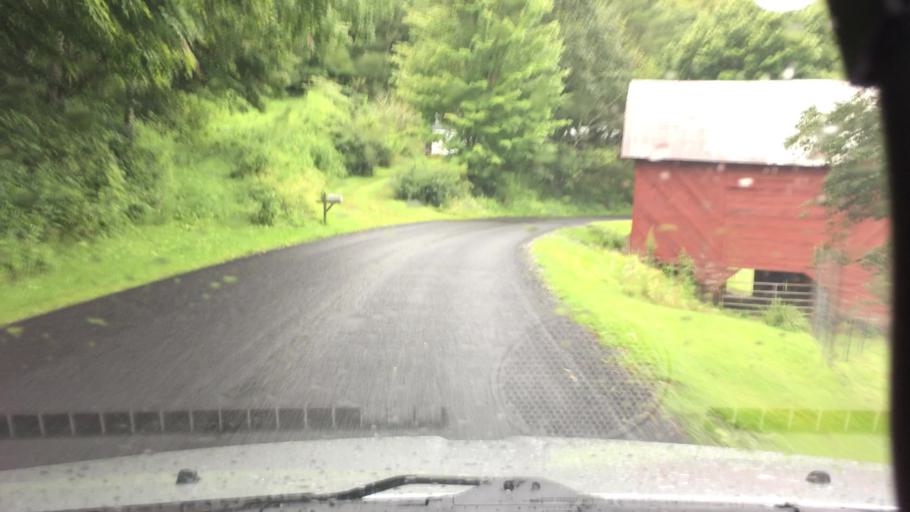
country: US
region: North Carolina
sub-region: Madison County
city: Mars Hill
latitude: 35.9104
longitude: -82.5321
